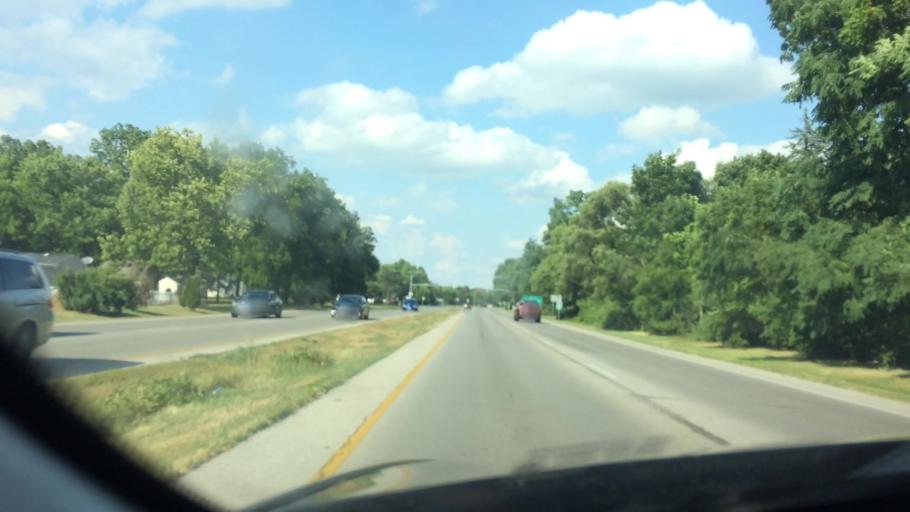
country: US
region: Ohio
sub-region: Lucas County
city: Maumee
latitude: 41.5692
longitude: -83.6465
